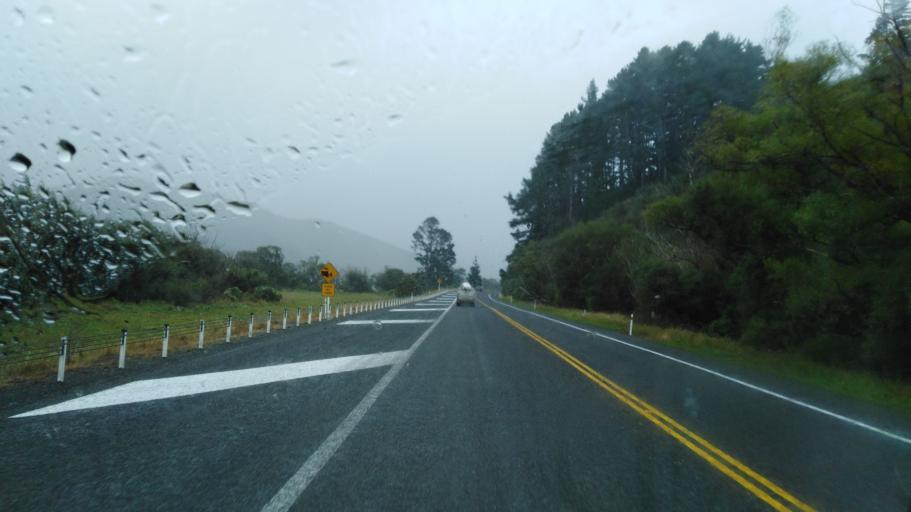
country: NZ
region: Marlborough
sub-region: Marlborough District
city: Picton
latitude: -41.3762
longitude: 173.9468
